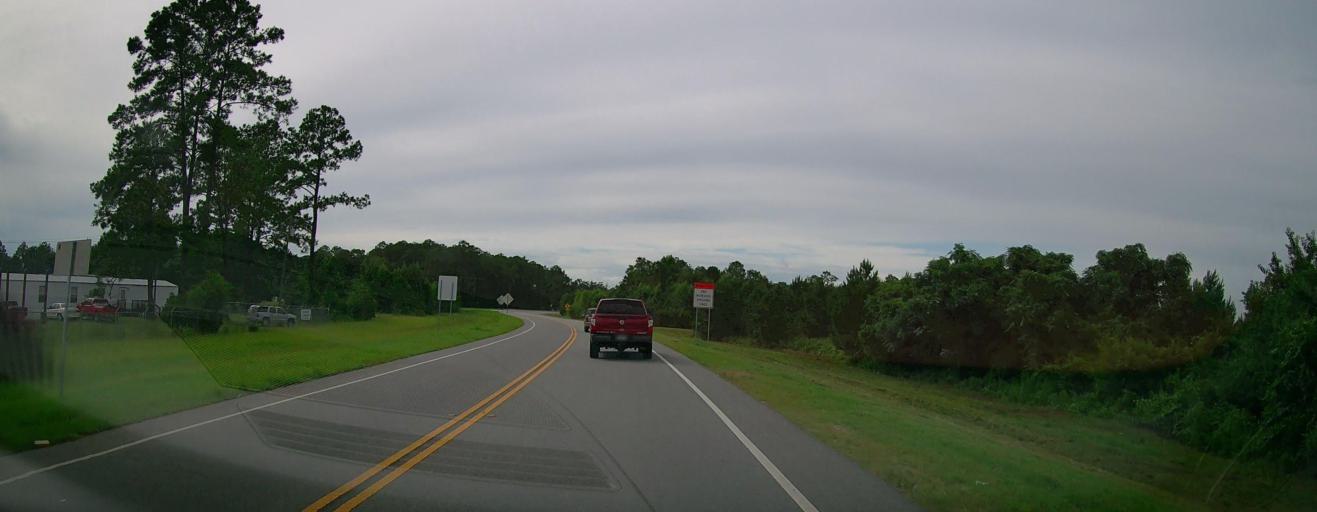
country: US
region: Georgia
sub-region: Wayne County
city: Jesup
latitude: 31.6214
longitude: -81.8953
